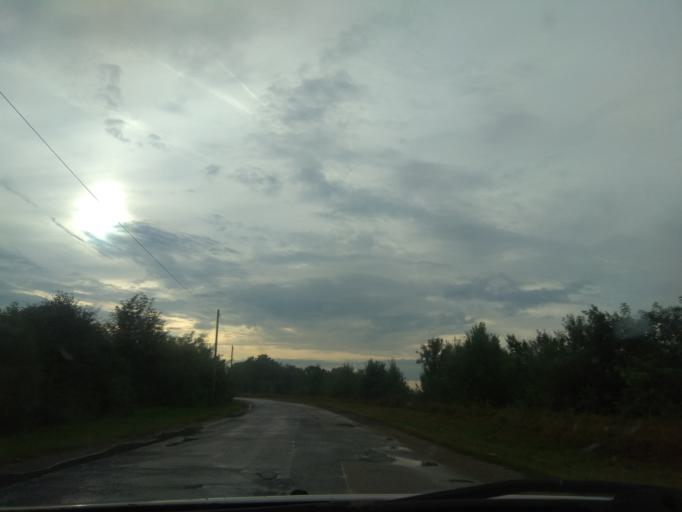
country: HU
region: Borsod-Abauj-Zemplen
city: Onga
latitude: 48.1200
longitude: 20.9255
